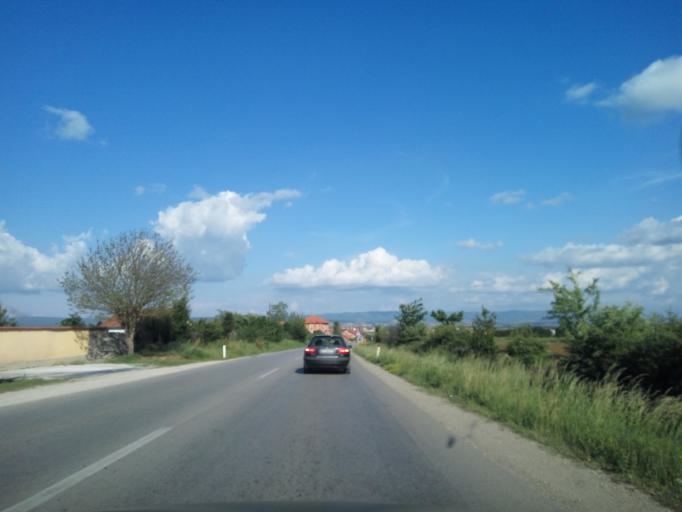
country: XK
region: Prizren
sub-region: Komuna e Malisheves
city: Llazice
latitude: 42.5865
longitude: 20.6852
